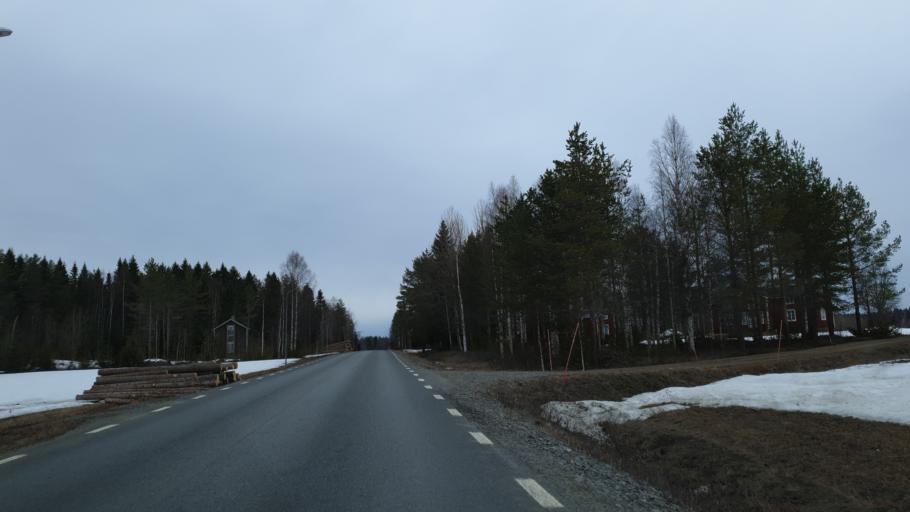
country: SE
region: Vaesterbotten
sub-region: Robertsfors Kommun
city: Robertsfors
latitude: 64.3852
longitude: 20.8973
